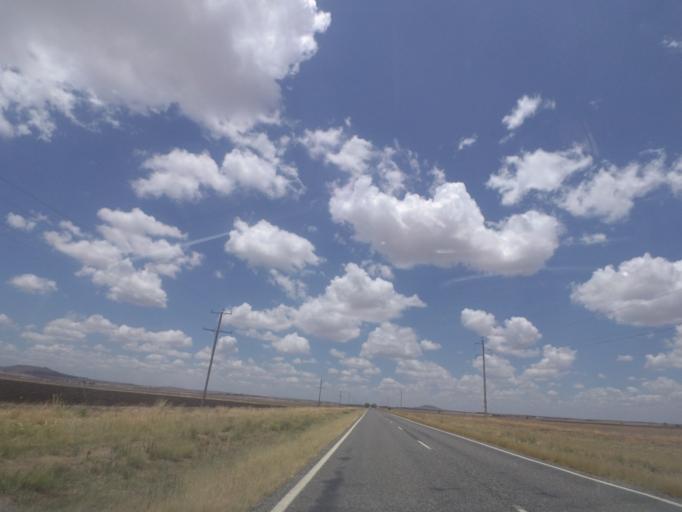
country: AU
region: Queensland
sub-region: Toowoomba
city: Top Camp
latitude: -27.9063
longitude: 151.9782
